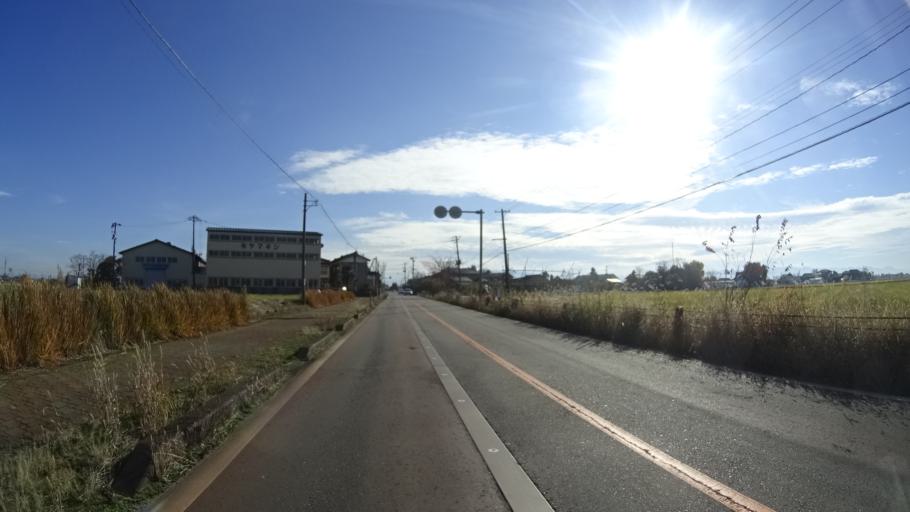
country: JP
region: Niigata
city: Mitsuke
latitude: 37.5522
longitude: 138.8645
